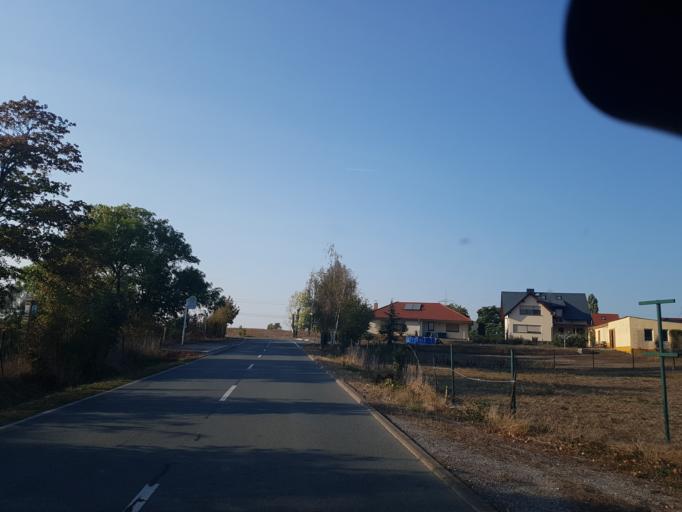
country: DE
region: Saxony
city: Strehla
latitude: 51.3181
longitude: 13.2184
